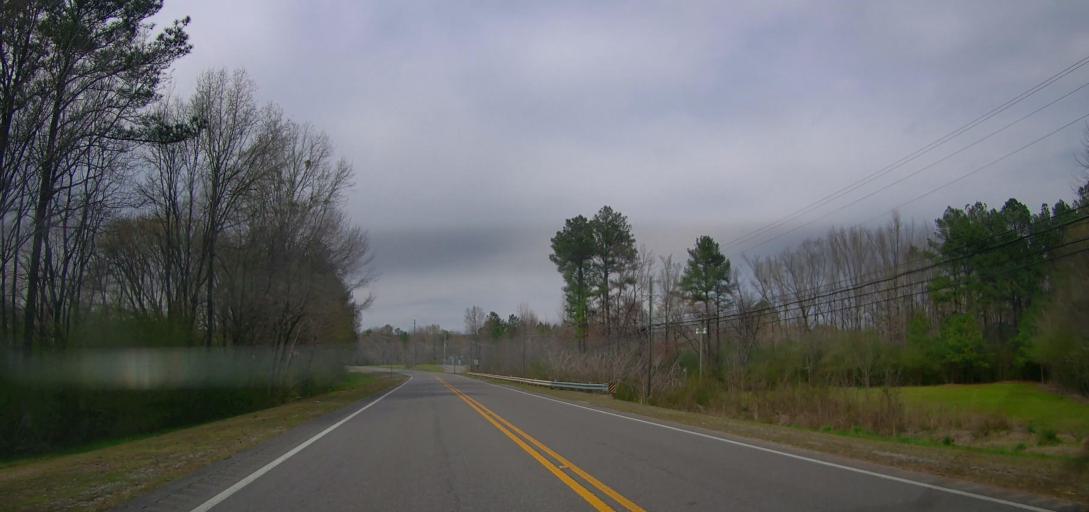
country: US
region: Alabama
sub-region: Walker County
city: Carbon Hill
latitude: 33.8948
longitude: -87.5362
